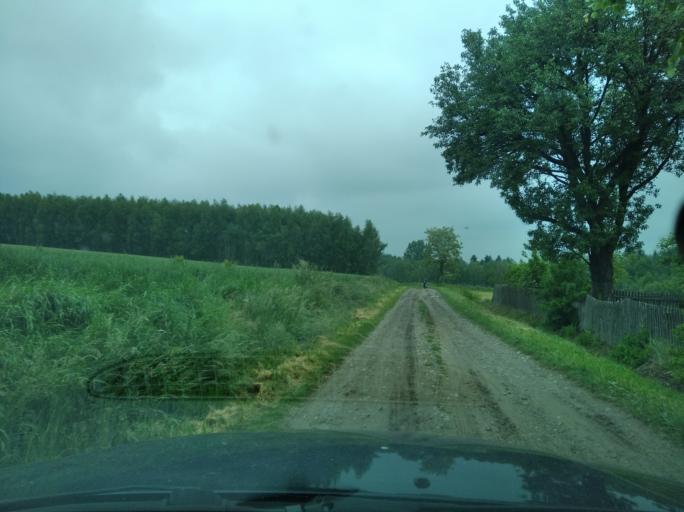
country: PL
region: Subcarpathian Voivodeship
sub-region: Powiat ropczycko-sedziszowski
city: Zagorzyce
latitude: 49.9813
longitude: 21.7084
